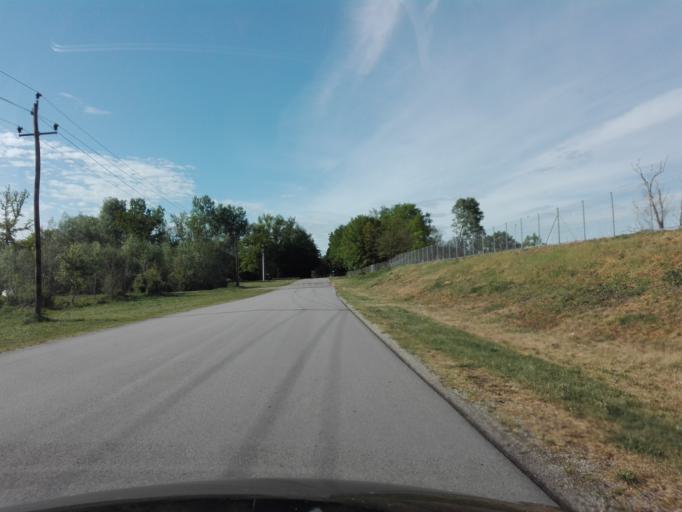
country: AT
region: Upper Austria
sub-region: Politischer Bezirk Linz-Land
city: Asten
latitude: 48.2395
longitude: 14.4159
